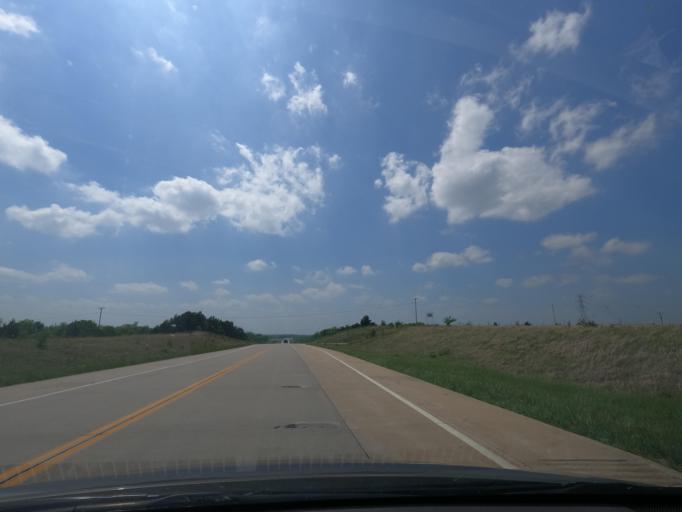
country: US
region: Kansas
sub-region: Wilson County
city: Fredonia
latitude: 37.6195
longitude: -96.0186
